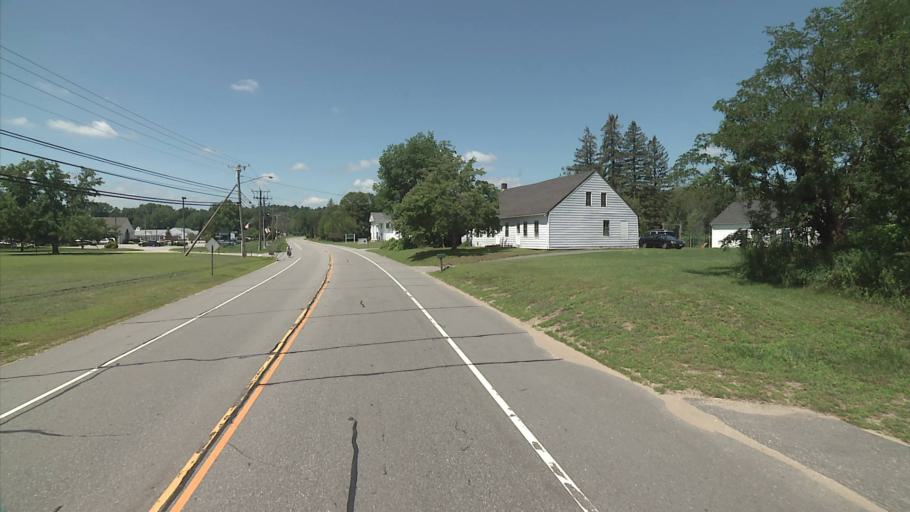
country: US
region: Connecticut
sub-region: Windham County
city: Plainfield Village
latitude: 41.6980
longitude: -71.9932
